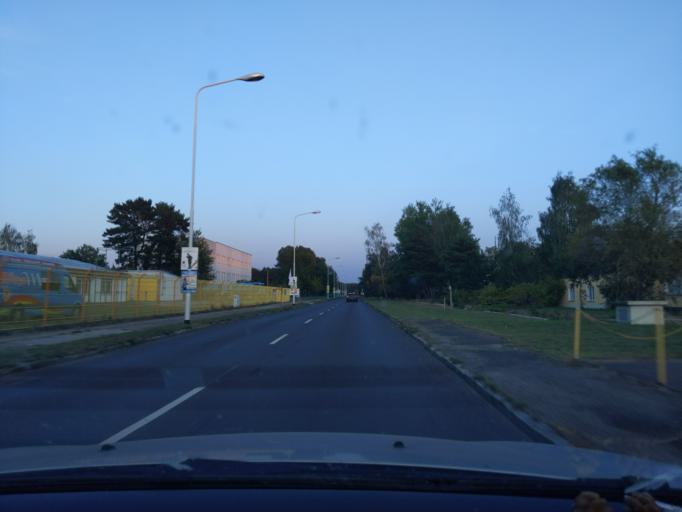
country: DE
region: Saxony
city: Hoyerswerda
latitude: 51.4305
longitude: 14.2880
